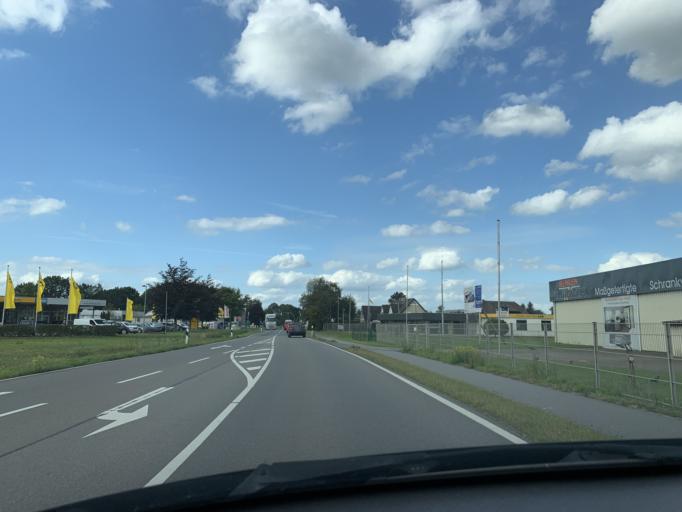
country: DE
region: Lower Saxony
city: Bad Zwischenahn
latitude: 53.1686
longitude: 7.9999
